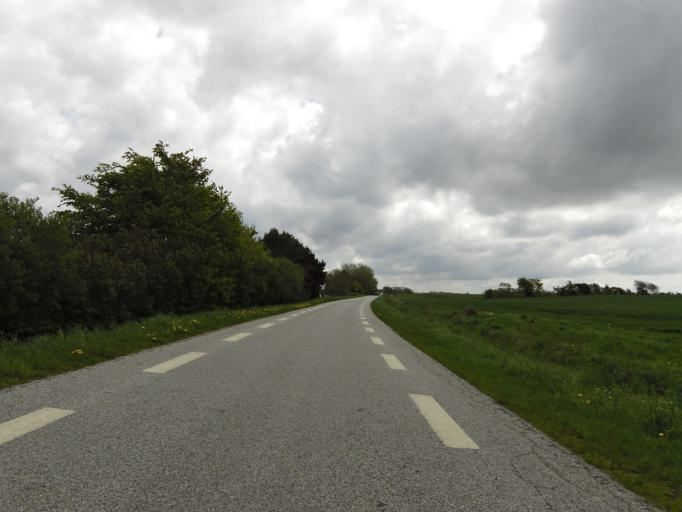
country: DK
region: South Denmark
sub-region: Haderslev Kommune
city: Gram
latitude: 55.2410
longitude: 8.9749
